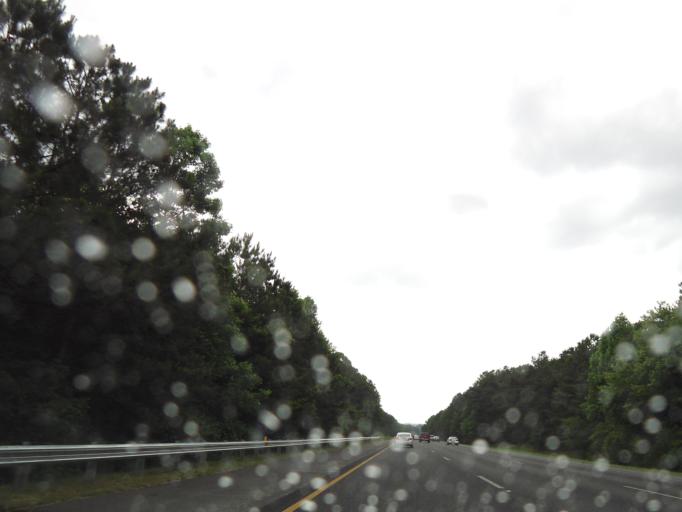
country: US
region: Georgia
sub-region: Carroll County
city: Villa Rica
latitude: 33.7231
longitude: -84.8811
